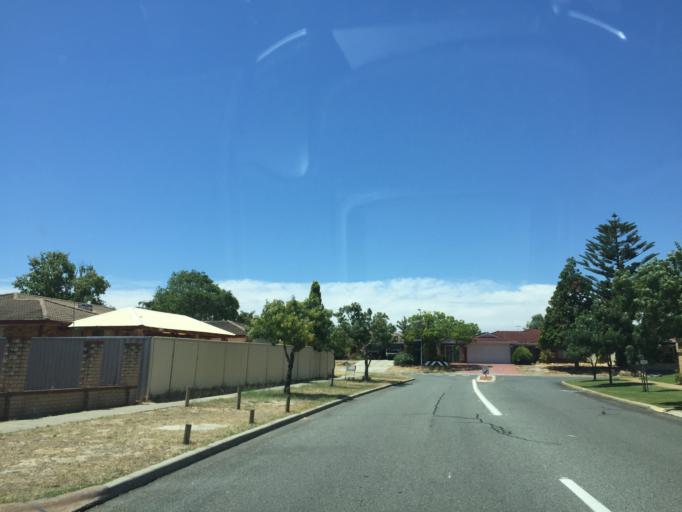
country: AU
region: Western Australia
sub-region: Melville
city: Winthrop
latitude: -32.0630
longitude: 115.8363
